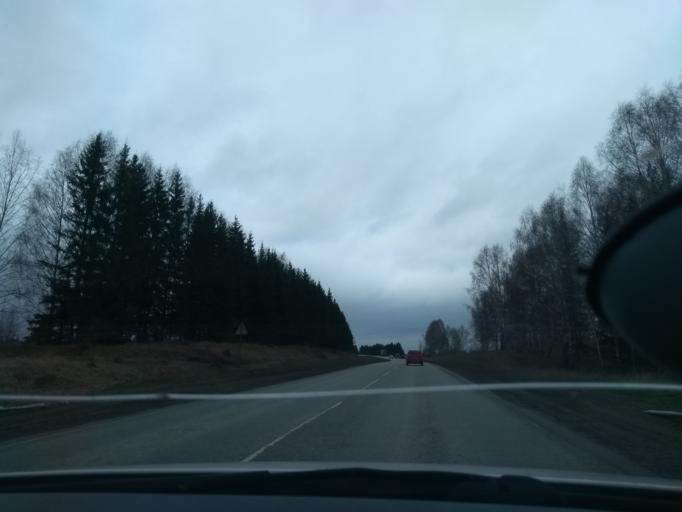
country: RU
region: Perm
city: Kungur
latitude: 57.4695
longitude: 56.7495
